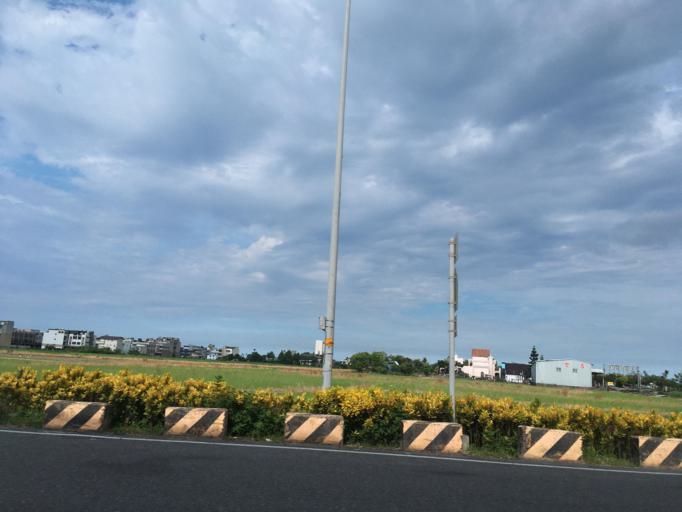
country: TW
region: Taiwan
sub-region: Yilan
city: Yilan
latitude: 24.6807
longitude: 121.7935
